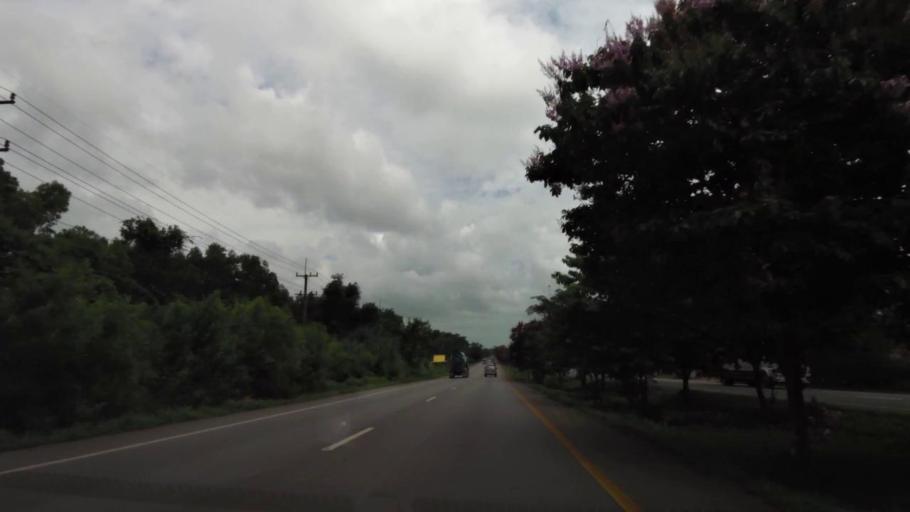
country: TH
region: Chanthaburi
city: Na Yai Am
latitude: 12.7466
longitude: 101.8805
